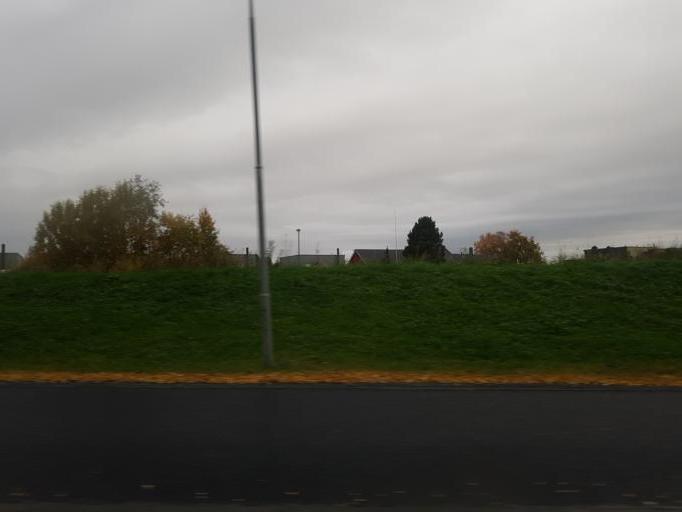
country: NO
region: Sor-Trondelag
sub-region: Trondheim
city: Trondheim
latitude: 63.3708
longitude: 10.3583
